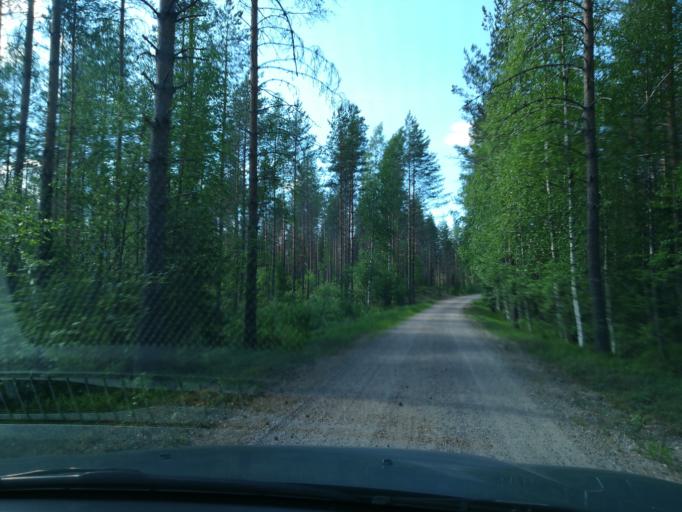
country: FI
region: South Karelia
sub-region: Imatra
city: Ruokolahti
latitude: 61.5362
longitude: 28.8328
